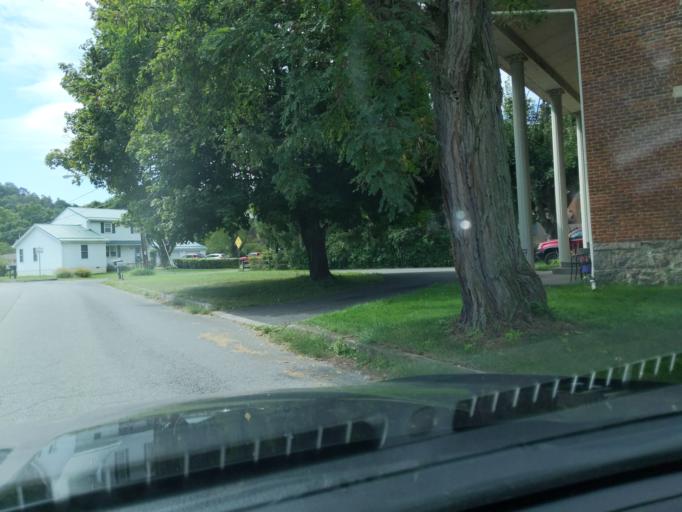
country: US
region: Pennsylvania
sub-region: Blair County
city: Duncansville
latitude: 40.4265
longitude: -78.4277
